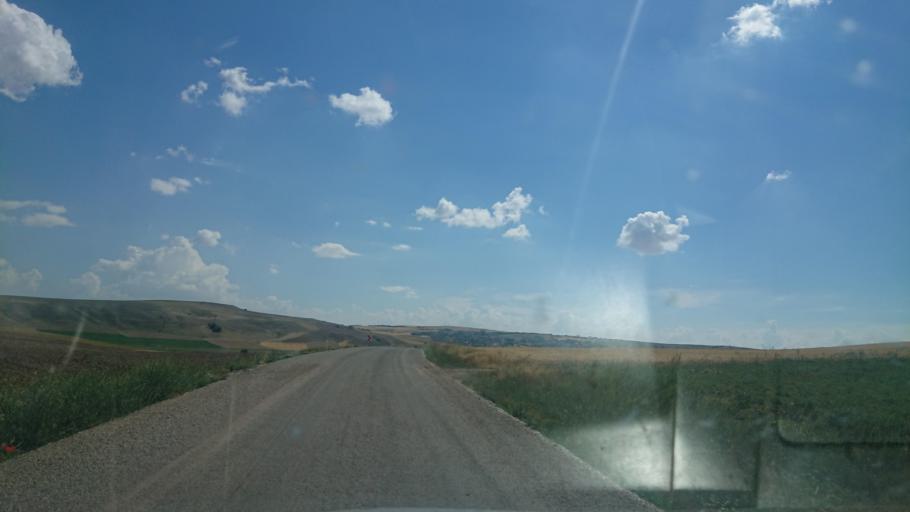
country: TR
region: Aksaray
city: Agacoren
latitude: 38.7877
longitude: 33.8109
